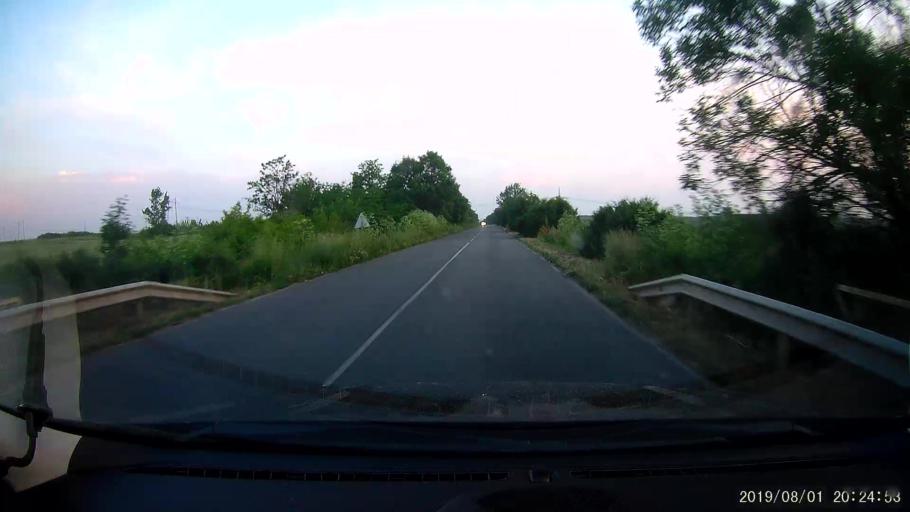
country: BG
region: Yambol
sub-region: Obshtina Elkhovo
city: Elkhovo
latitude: 42.2245
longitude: 26.5908
